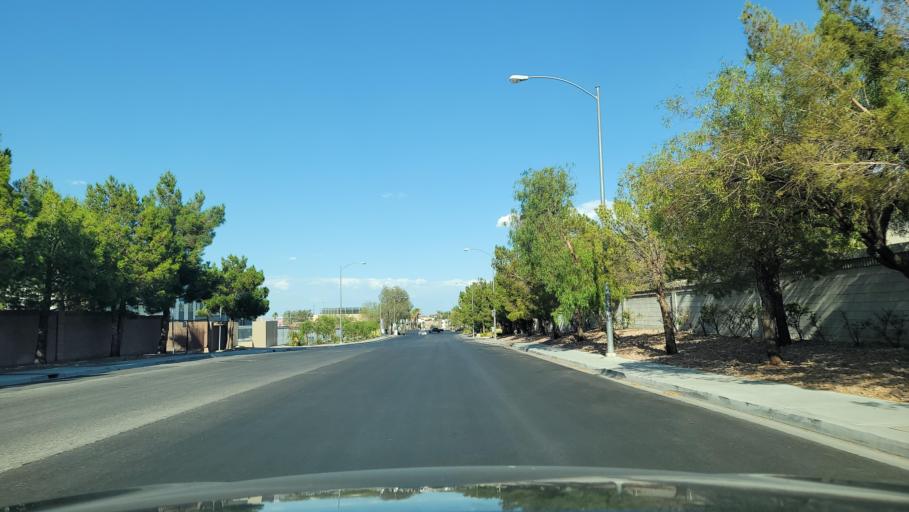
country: US
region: Nevada
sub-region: Clark County
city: Summerlin South
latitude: 36.0963
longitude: -115.3002
